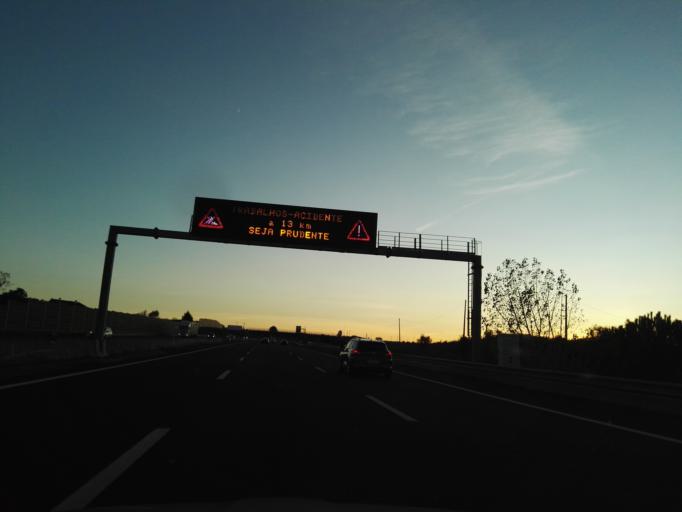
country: PT
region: Santarem
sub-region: Cartaxo
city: Pontevel
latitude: 39.1583
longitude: -8.8658
